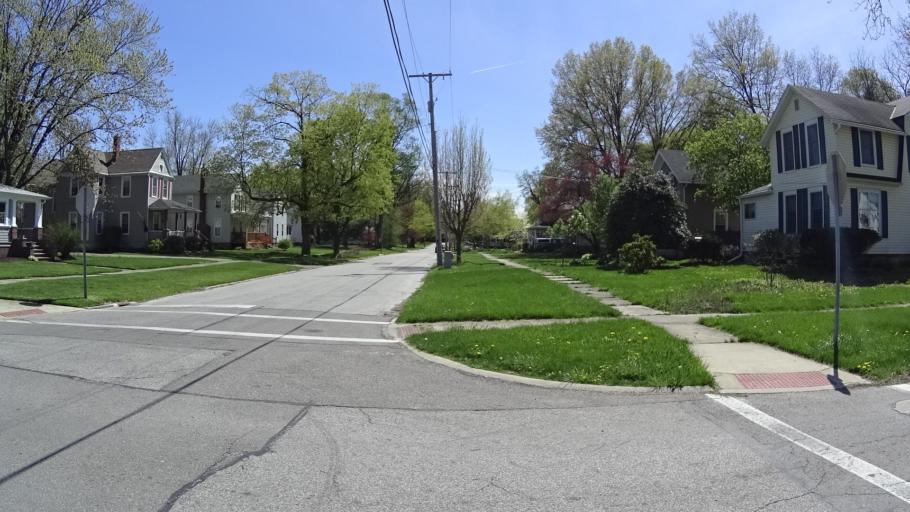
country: US
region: Ohio
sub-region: Lorain County
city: Elyria
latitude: 41.3752
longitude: -82.1000
